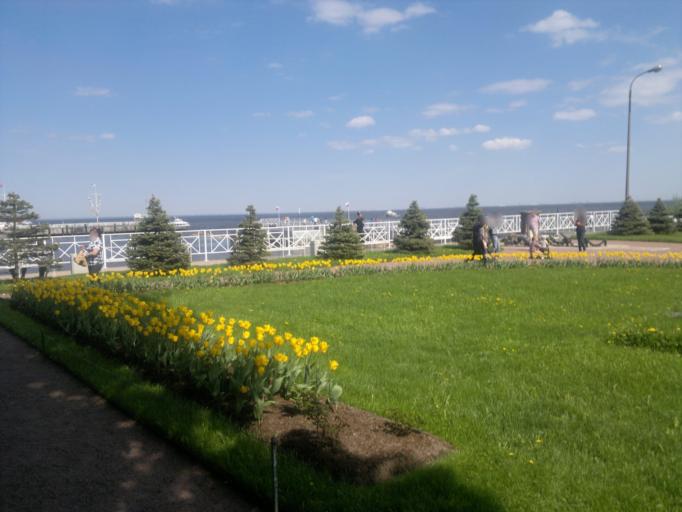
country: RU
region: St.-Petersburg
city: Peterhof
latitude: 59.8902
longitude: 29.9127
